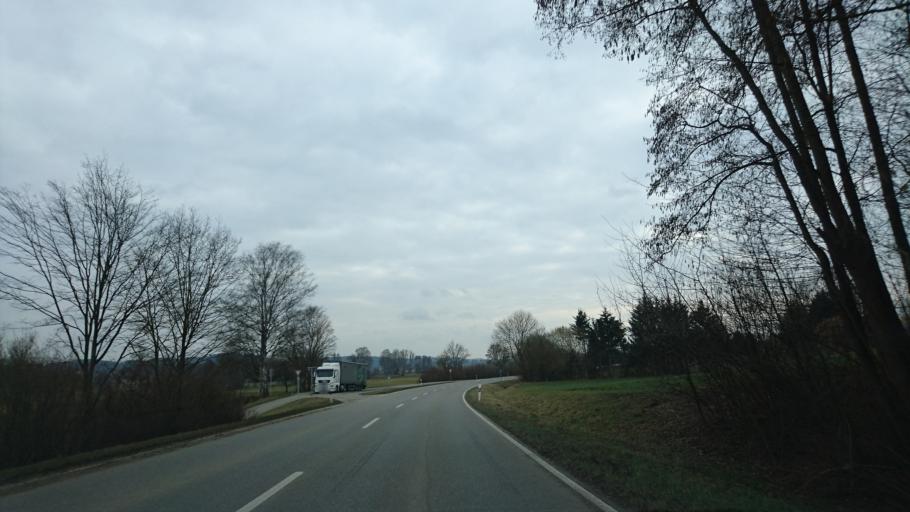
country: DE
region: Bavaria
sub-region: Swabia
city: Altenmunster
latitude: 48.4568
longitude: 10.5880
